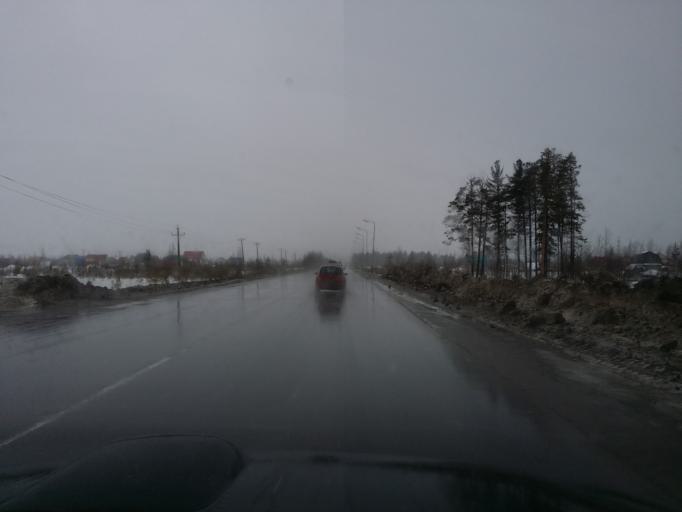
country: RU
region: Khanty-Mansiyskiy Avtonomnyy Okrug
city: Nizhnevartovsk
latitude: 60.9517
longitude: 76.6886
